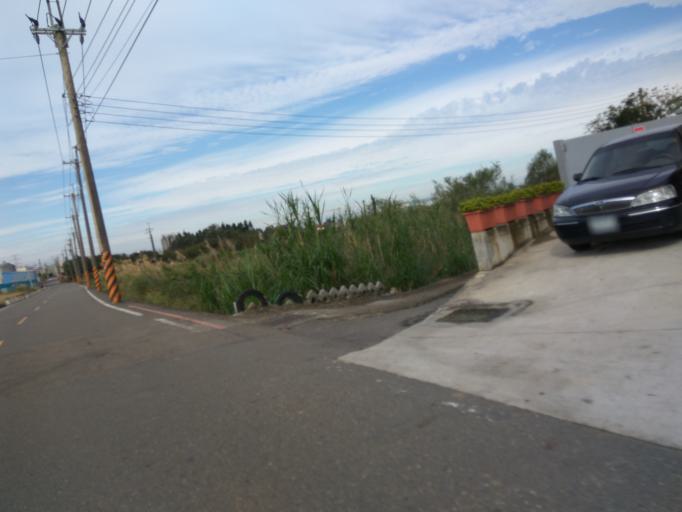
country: TW
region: Taiwan
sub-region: Hsinchu
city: Zhubei
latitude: 24.9597
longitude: 121.1040
